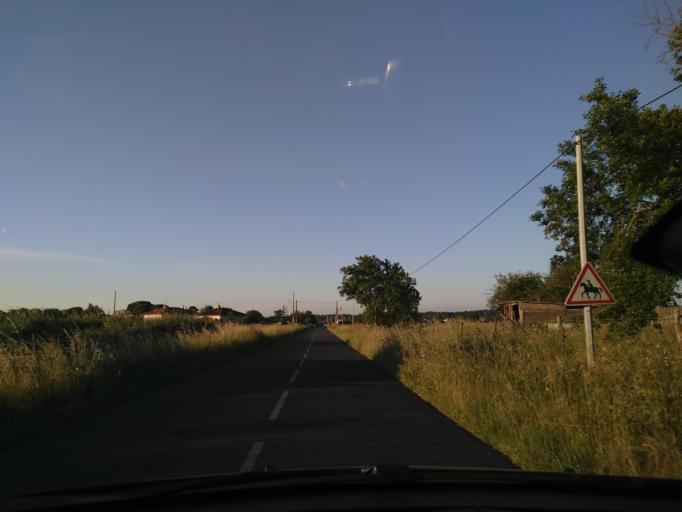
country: FR
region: Midi-Pyrenees
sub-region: Departement de la Haute-Garonne
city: Grenade
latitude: 43.7537
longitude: 1.2856
